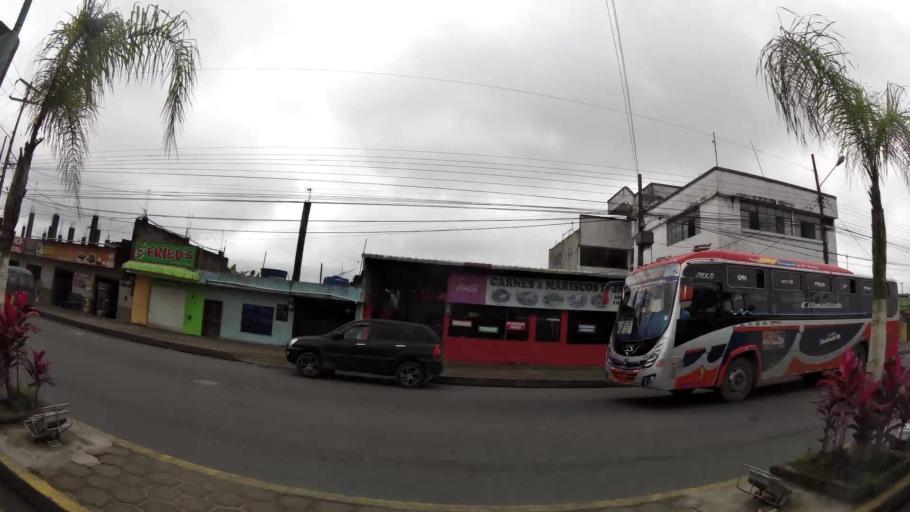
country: EC
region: Santo Domingo de los Tsachilas
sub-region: Canton Santo Domingo de los Colorados
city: Santo Domingo de los Colorados
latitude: -0.2541
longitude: -79.1969
